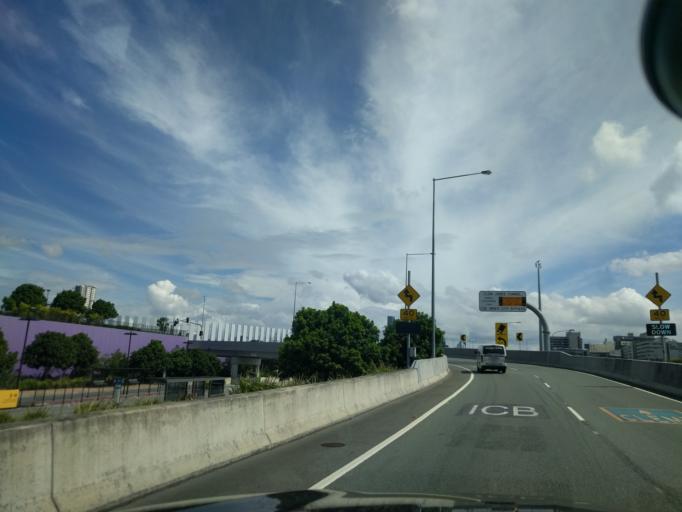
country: AU
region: Queensland
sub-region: Brisbane
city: Windsor
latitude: -27.4407
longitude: 153.0309
